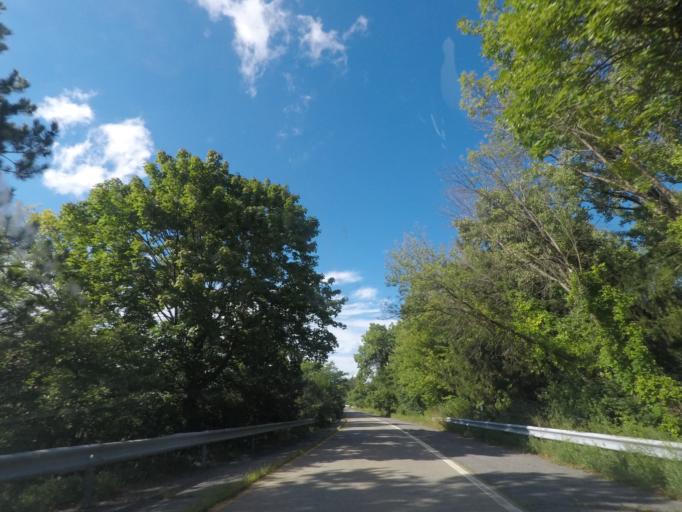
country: US
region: New York
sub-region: Albany County
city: Albany
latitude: 42.6728
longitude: -73.7462
